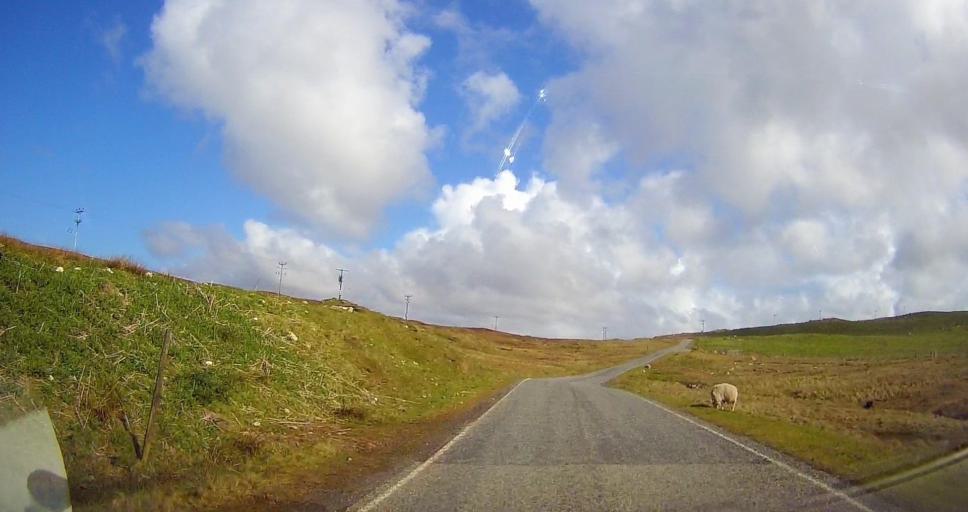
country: GB
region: Scotland
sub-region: Shetland Islands
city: Lerwick
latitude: 60.4785
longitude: -1.4065
